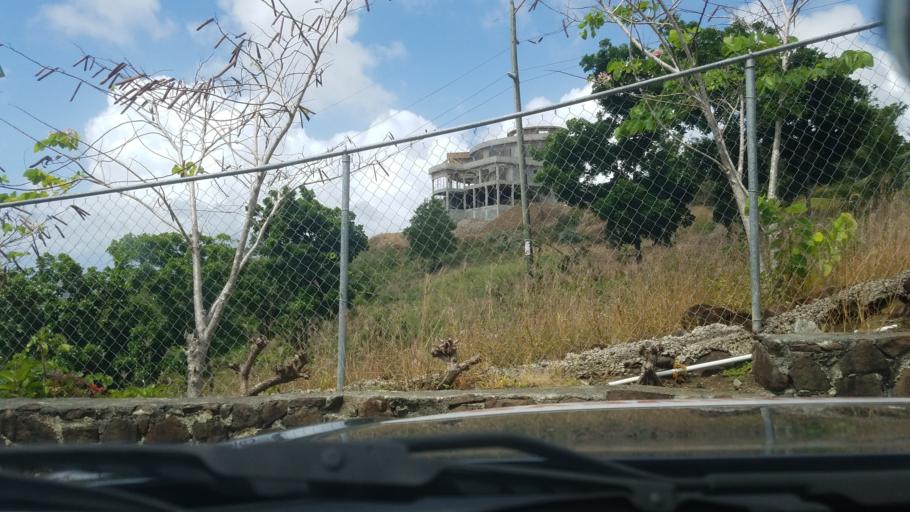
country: LC
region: Gros-Islet
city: Gros Islet
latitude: 14.0634
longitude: -60.9495
